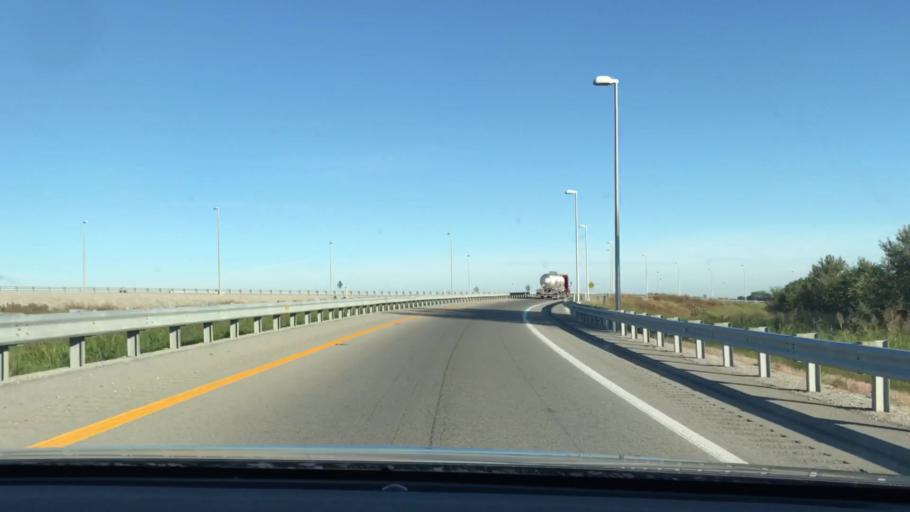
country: US
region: Kentucky
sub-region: Christian County
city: Fort Campbell North
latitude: 36.7443
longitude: -87.5098
